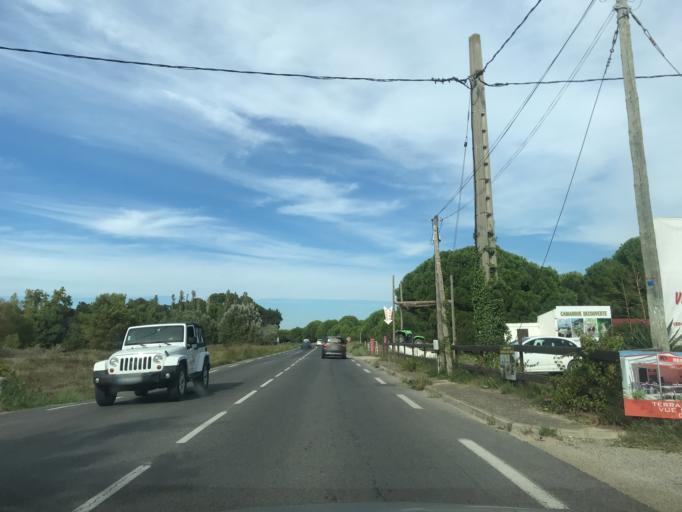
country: FR
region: Languedoc-Roussillon
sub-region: Departement du Gard
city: Aigues-Mortes
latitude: 43.5825
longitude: 4.2073
